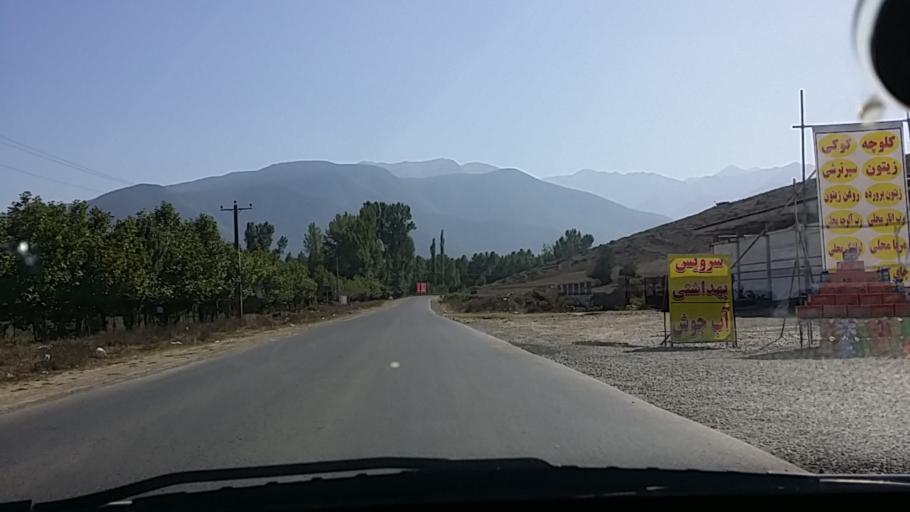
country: IR
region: Mazandaran
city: `Abbasabad
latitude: 36.5342
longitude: 51.1806
